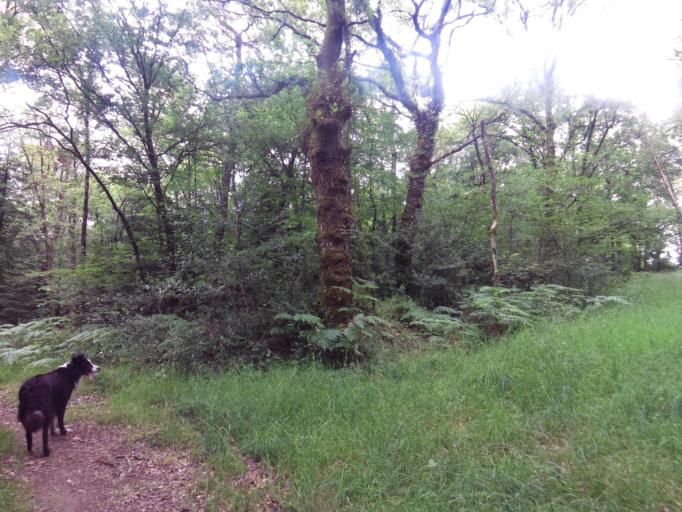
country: FR
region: Brittany
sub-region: Departement du Morbihan
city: Molac
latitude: 47.7625
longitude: -2.4288
